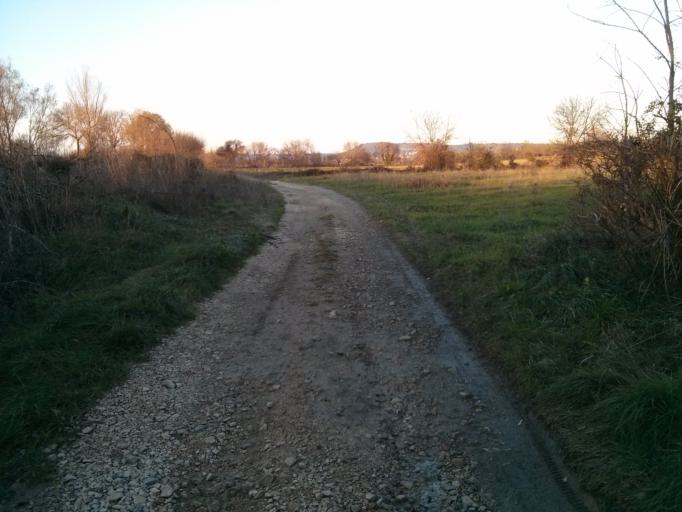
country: FR
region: Languedoc-Roussillon
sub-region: Departement du Gard
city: Vergeze
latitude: 43.7591
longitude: 4.2135
